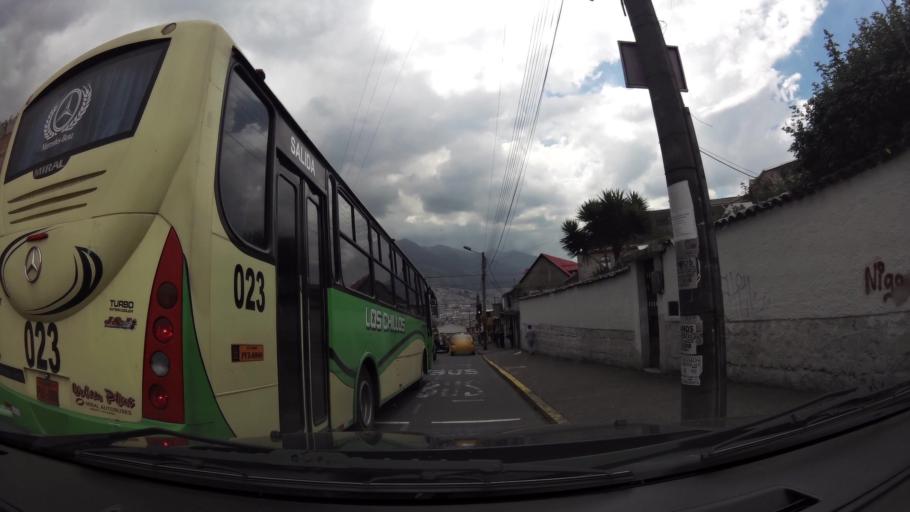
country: EC
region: Pichincha
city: Quito
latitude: -0.2426
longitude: -78.5063
